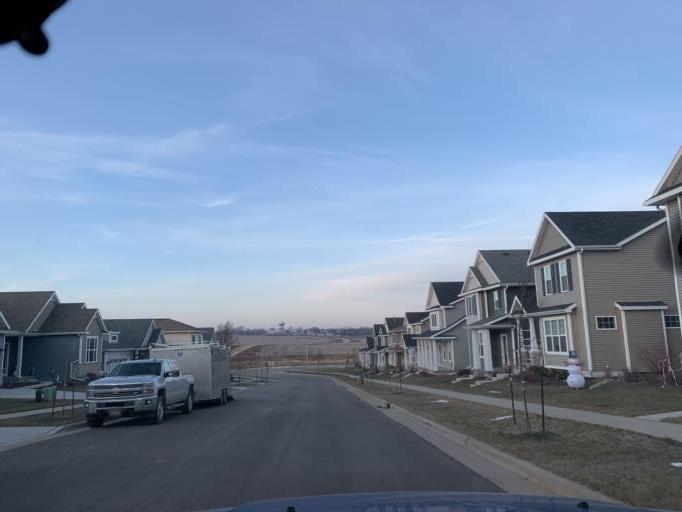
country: US
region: Wisconsin
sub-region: Dane County
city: Middleton
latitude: 43.0577
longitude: -89.5662
